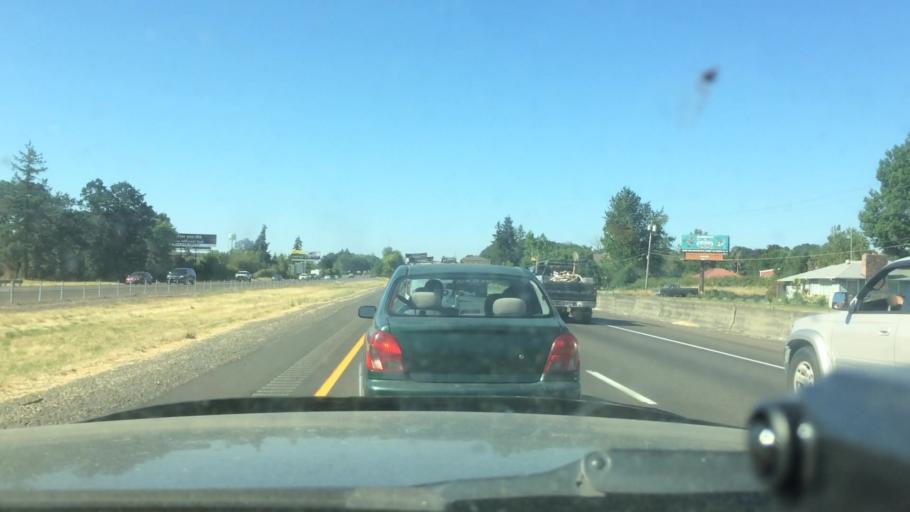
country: US
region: Oregon
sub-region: Linn County
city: Millersburg
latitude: 44.6565
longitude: -123.0605
